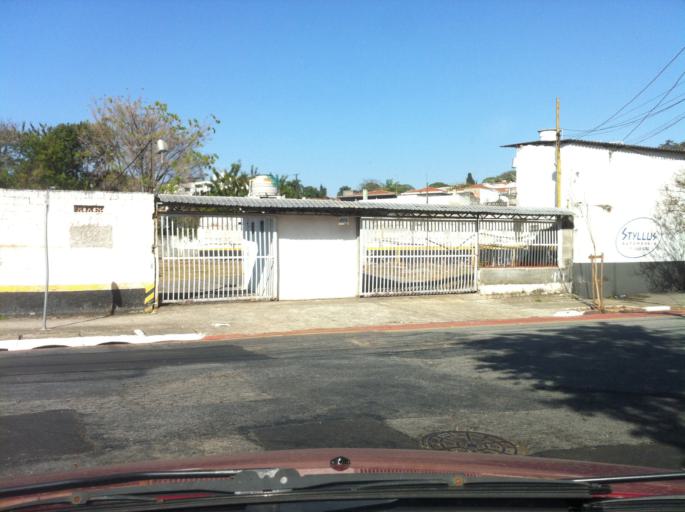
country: BR
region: Sao Paulo
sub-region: Sao Paulo
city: Sao Paulo
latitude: -23.6055
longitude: -46.6487
